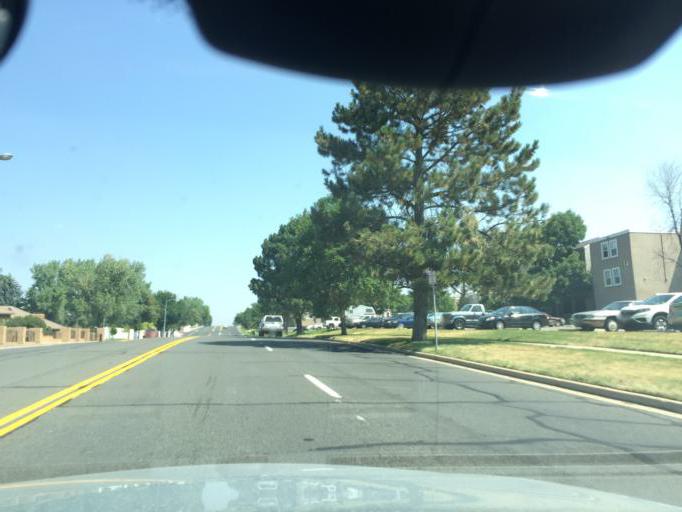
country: US
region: Colorado
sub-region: Adams County
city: Northglenn
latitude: 39.9046
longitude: -105.0061
